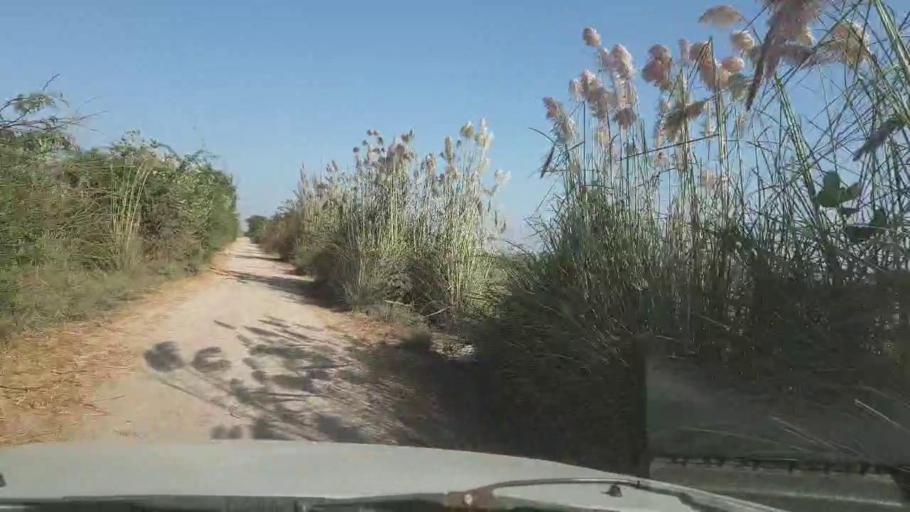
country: PK
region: Sindh
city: Mirpur Sakro
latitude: 24.4654
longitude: 67.7674
